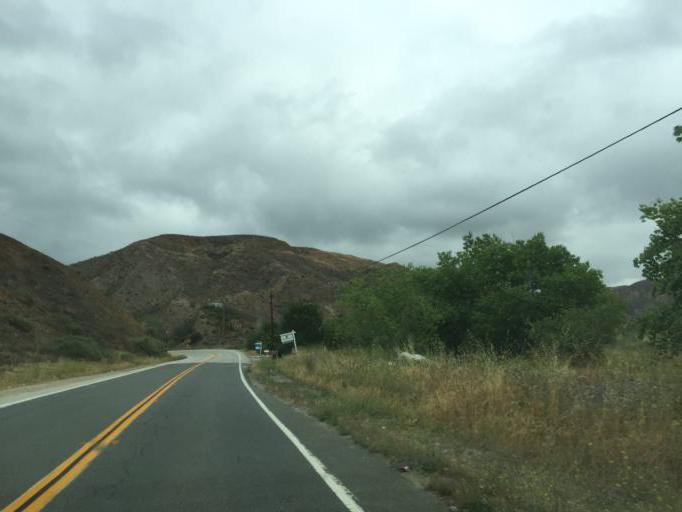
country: US
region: California
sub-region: Los Angeles County
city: Santa Clarita
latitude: 34.4927
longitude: -118.4598
